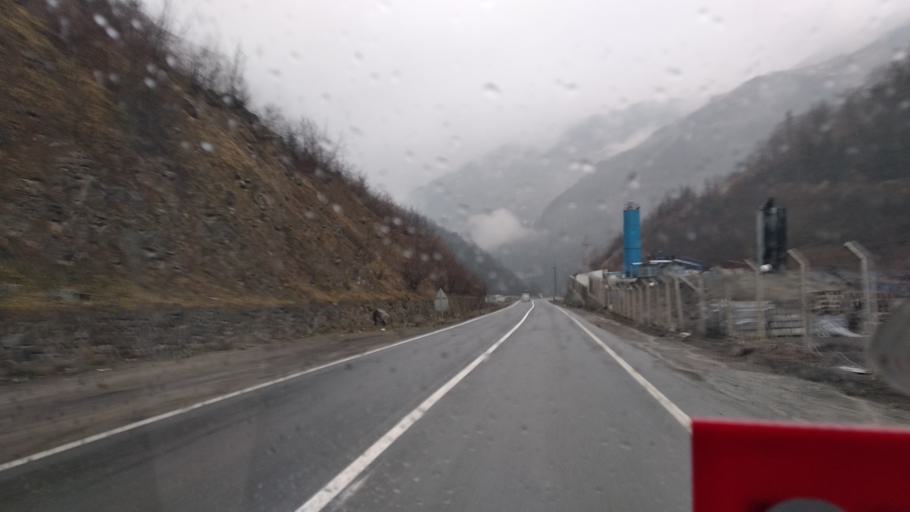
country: TR
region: Trabzon
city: Macka
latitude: 40.7421
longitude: 39.5530
